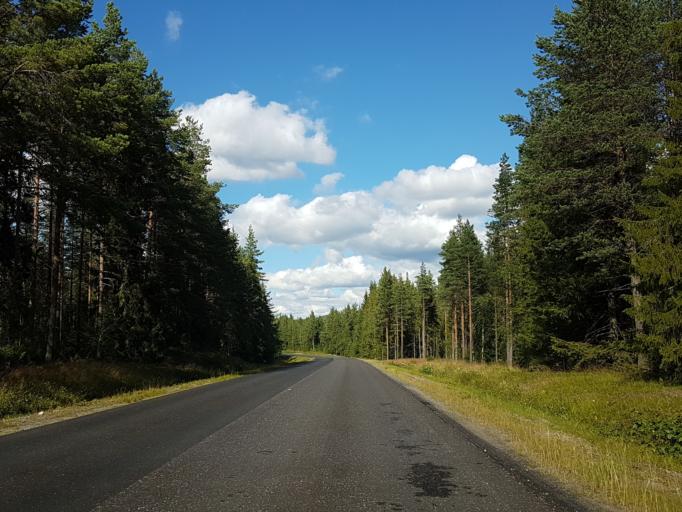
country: SE
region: Vaesterbotten
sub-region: Skelleftea Kommun
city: Burtraesk
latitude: 64.2947
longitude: 20.5254
